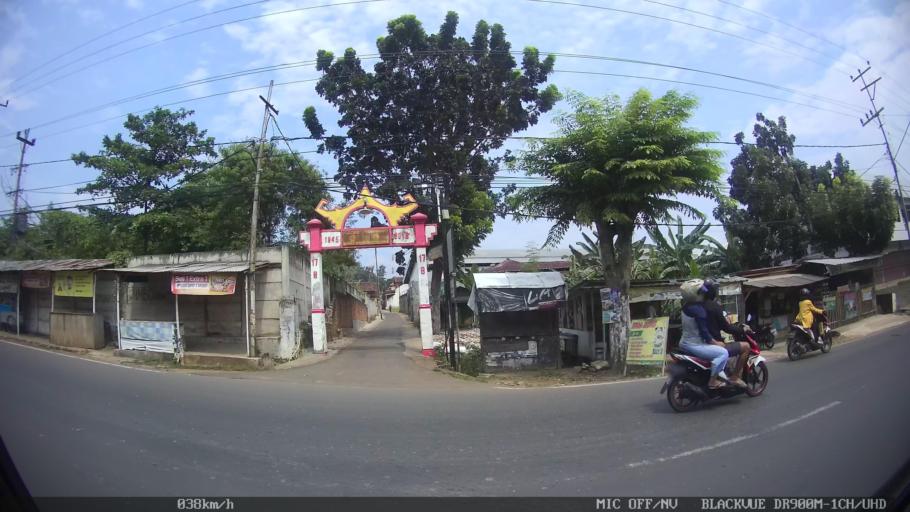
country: ID
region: Lampung
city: Bandarlampung
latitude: -5.4138
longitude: 105.2468
